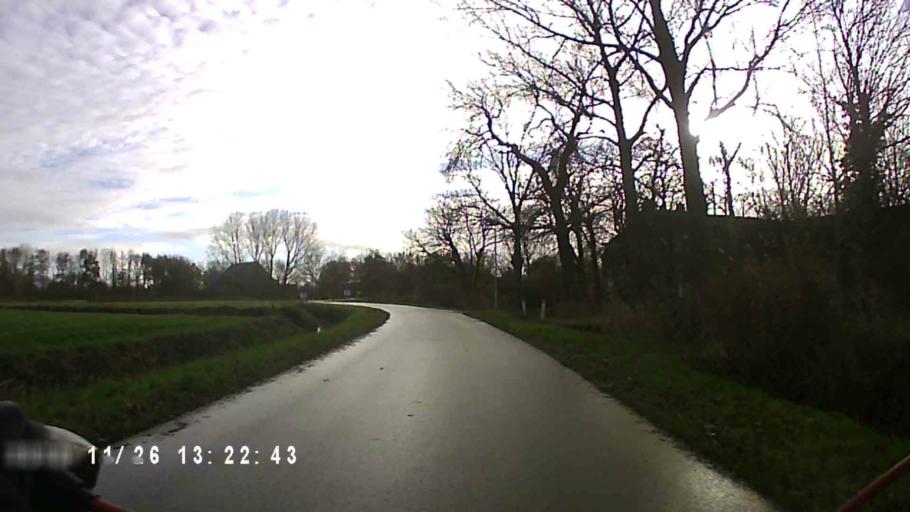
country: NL
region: Groningen
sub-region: Gemeente Delfzijl
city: Delfzijl
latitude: 53.3446
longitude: 6.8948
